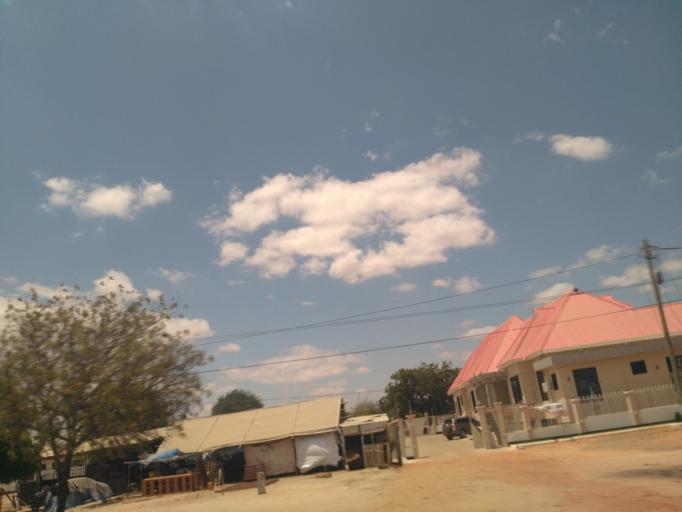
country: TZ
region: Dodoma
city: Kisasa
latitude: -6.1658
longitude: 35.7850
